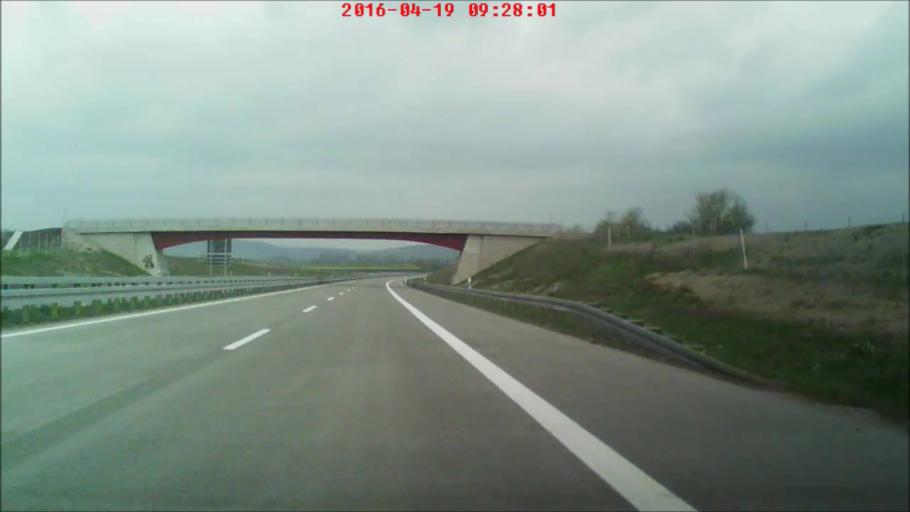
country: DE
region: Thuringia
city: Schillingstedt
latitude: 51.2255
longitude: 11.1838
